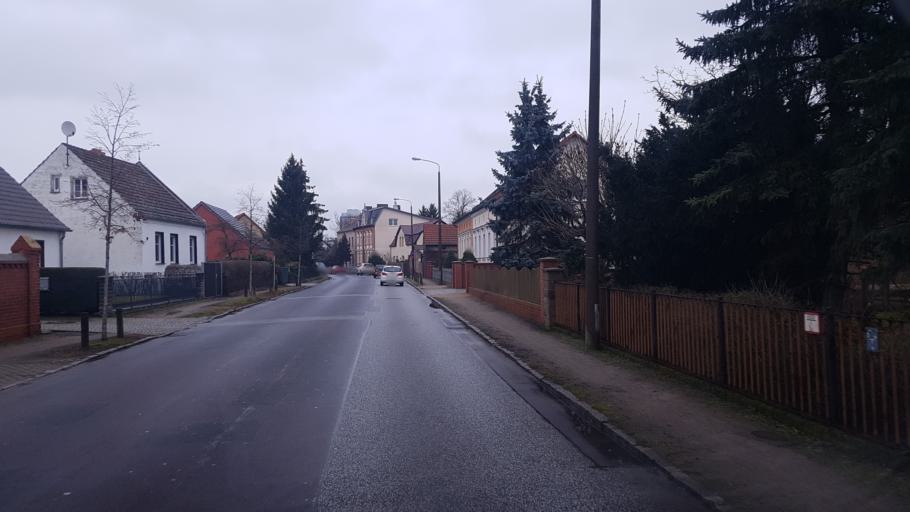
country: DE
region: Berlin
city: Wannsee
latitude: 52.3623
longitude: 13.1269
